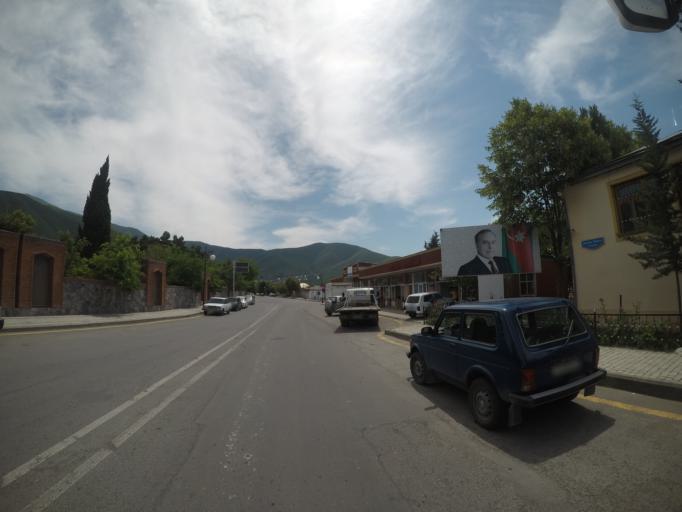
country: AZ
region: Shaki City
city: Sheki
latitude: 41.2066
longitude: 47.1680
